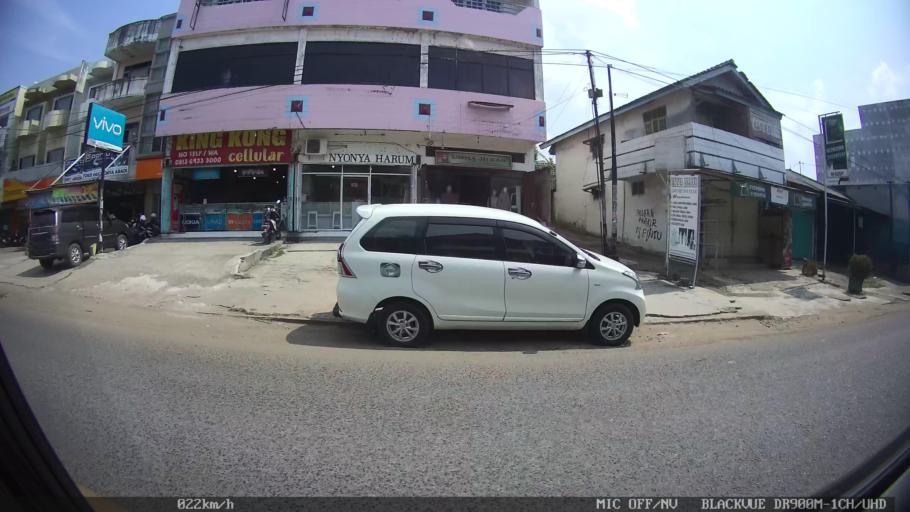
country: ID
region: Lampung
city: Pringsewu
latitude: -5.3559
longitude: 104.9782
